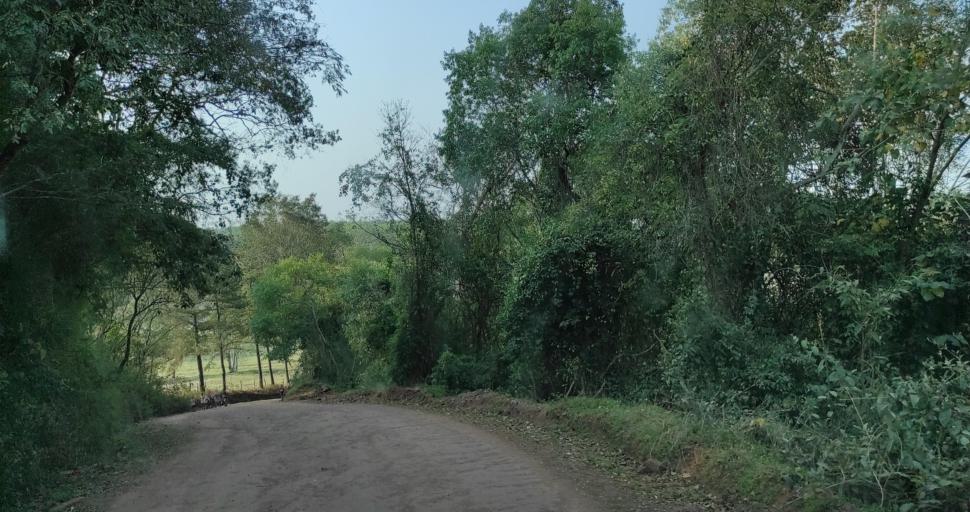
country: AR
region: Misiones
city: Cerro Azul
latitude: -27.6276
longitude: -55.4910
